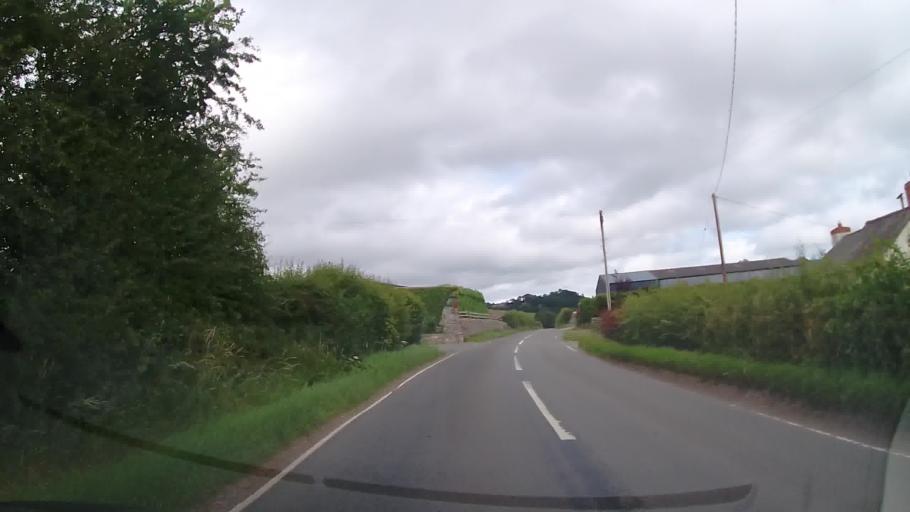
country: GB
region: Wales
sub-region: Sir Powys
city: Llanfechain
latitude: 52.8070
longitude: -3.1662
